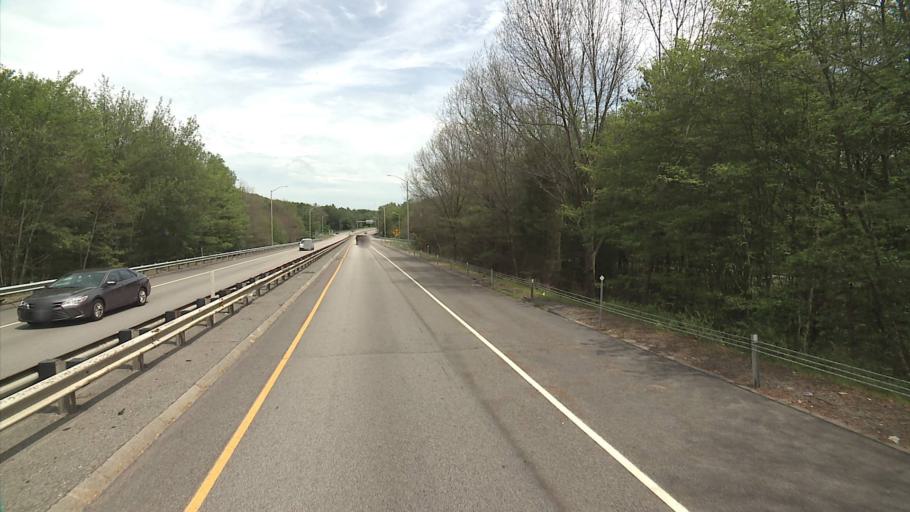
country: US
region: Connecticut
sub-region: New London County
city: Montville Center
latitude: 41.4872
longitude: -72.1141
